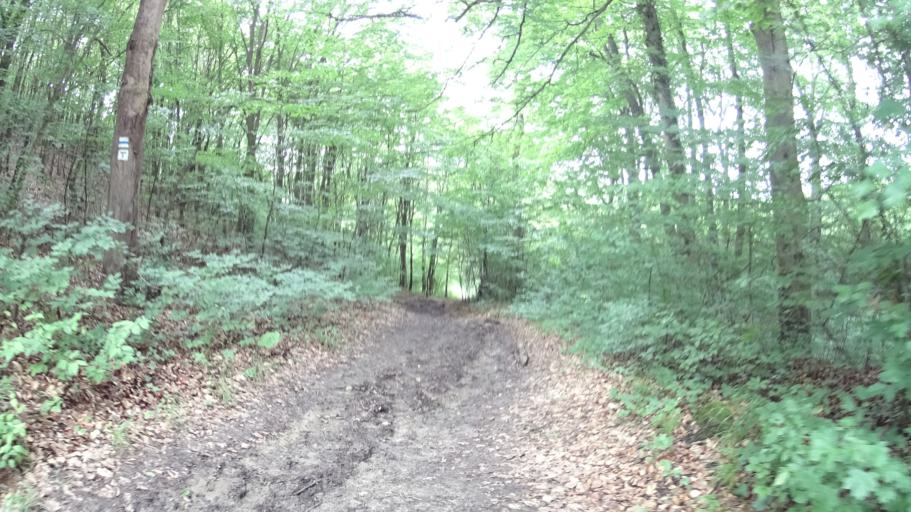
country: HU
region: Pest
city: Nagymaros
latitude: 47.8149
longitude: 18.9360
